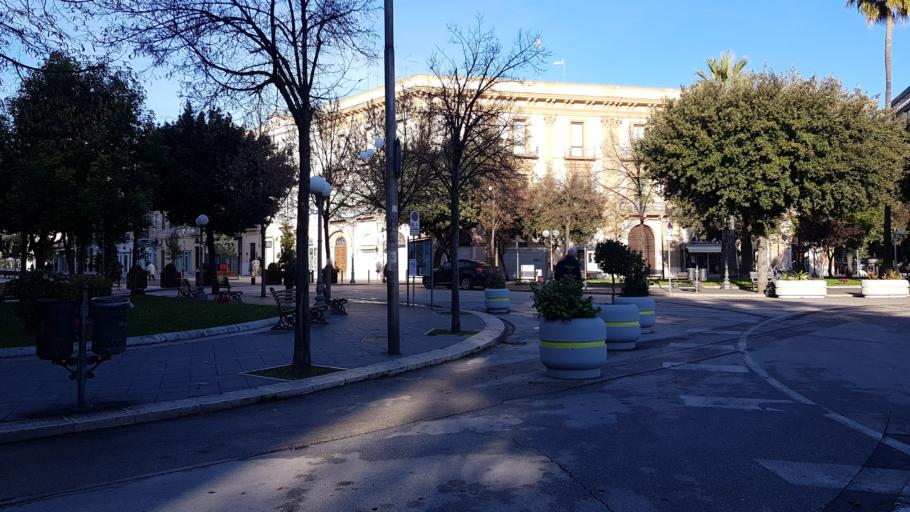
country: IT
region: Apulia
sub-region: Provincia di Foggia
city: Foggia
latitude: 41.4617
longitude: 15.5523
